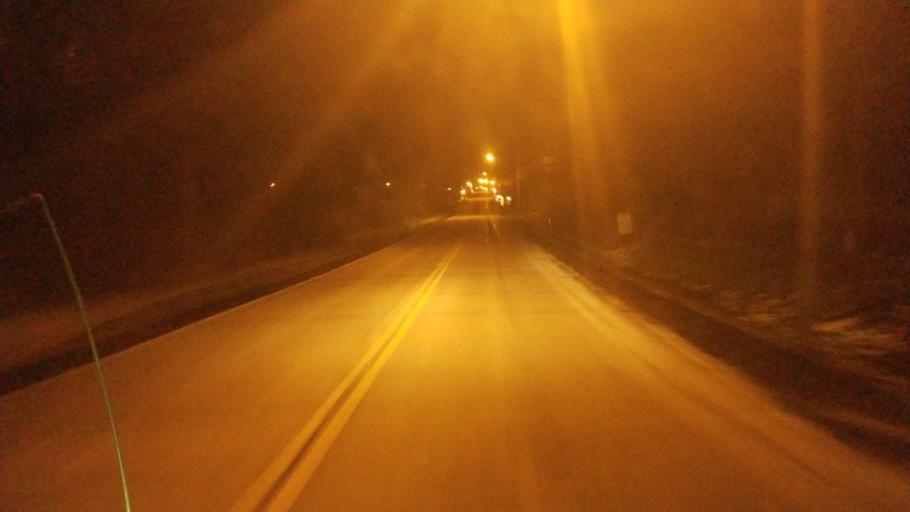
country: US
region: Ohio
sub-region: Cuyahoga County
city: Oakwood
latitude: 41.3570
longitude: -81.4744
